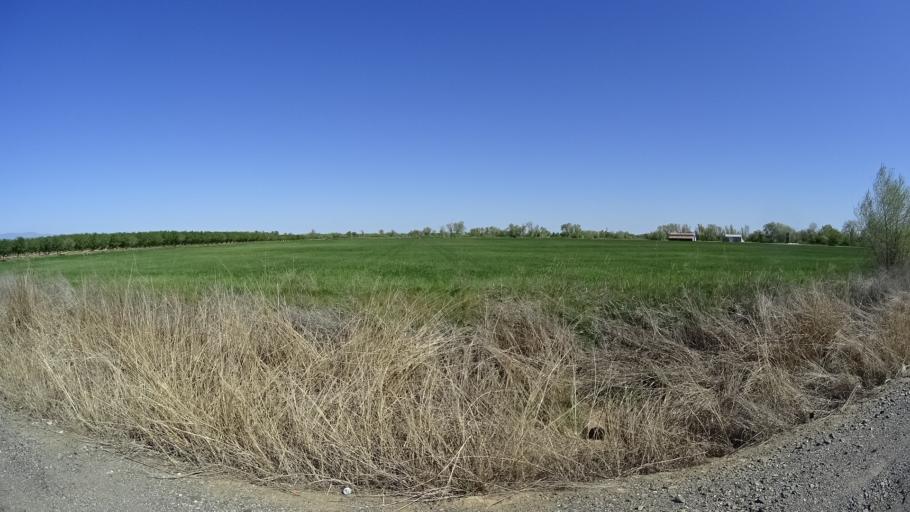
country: US
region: California
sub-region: Glenn County
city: Orland
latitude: 39.6972
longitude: -122.2321
